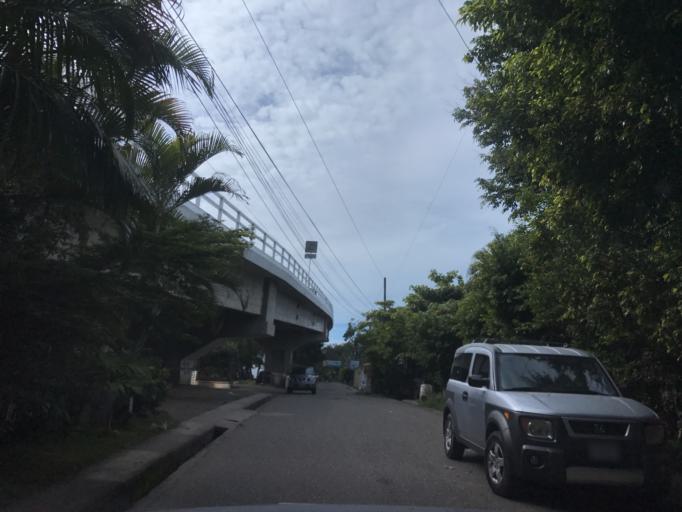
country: GT
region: Izabal
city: Morales
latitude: 15.6545
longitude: -88.9955
